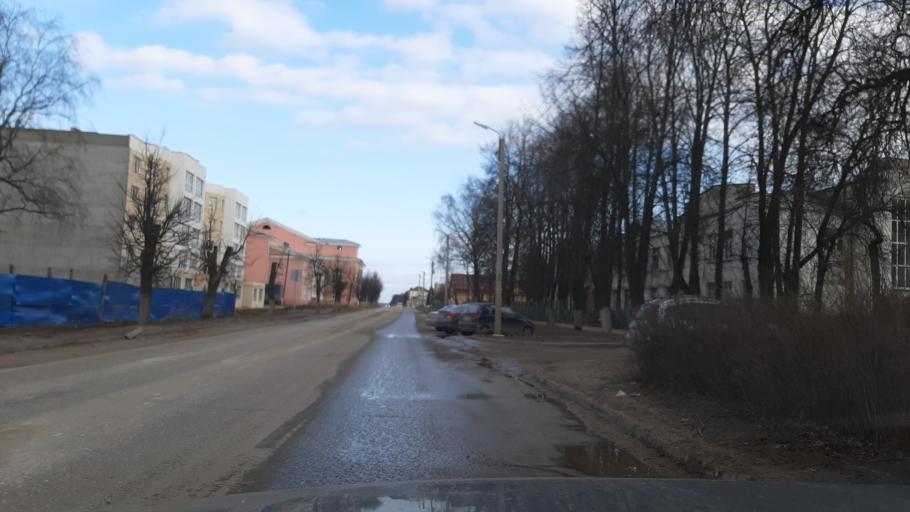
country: RU
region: Ivanovo
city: Teykovo
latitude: 56.8544
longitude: 40.5304
